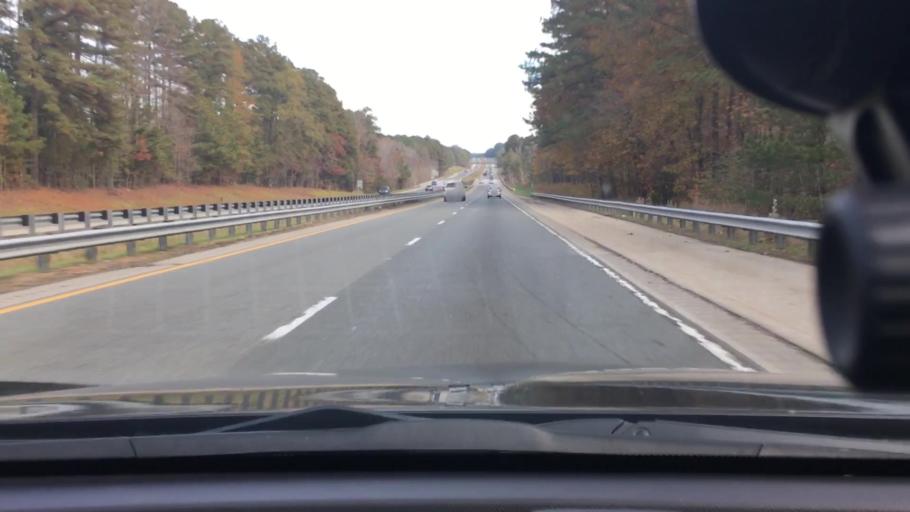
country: US
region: North Carolina
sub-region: Chatham County
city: Pittsboro
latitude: 35.6310
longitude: -79.0652
